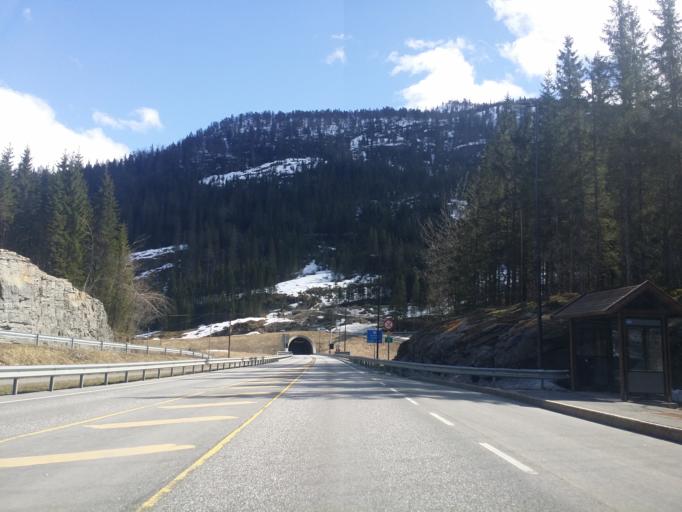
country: NO
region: Hordaland
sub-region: Granvin
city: Granvin
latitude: 60.5861
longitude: 6.6106
